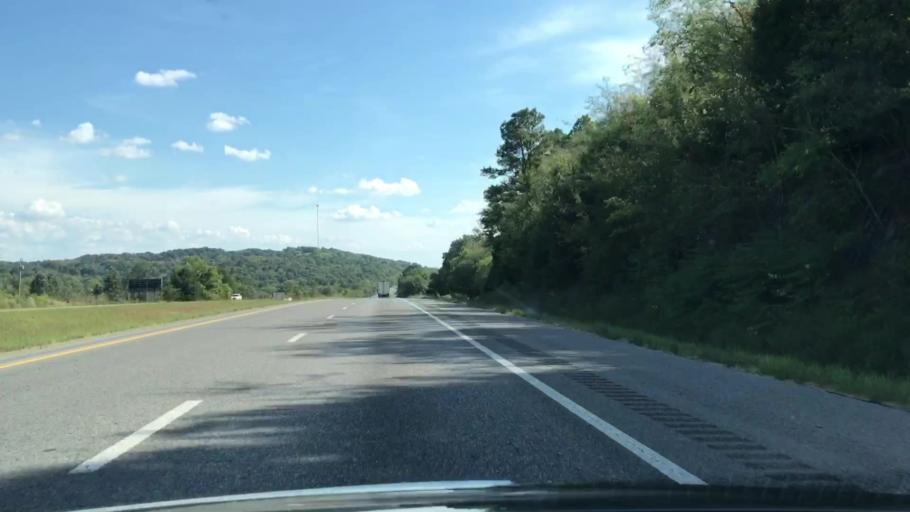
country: US
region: Alabama
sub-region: Limestone County
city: Ardmore
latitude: 35.0420
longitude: -86.8798
